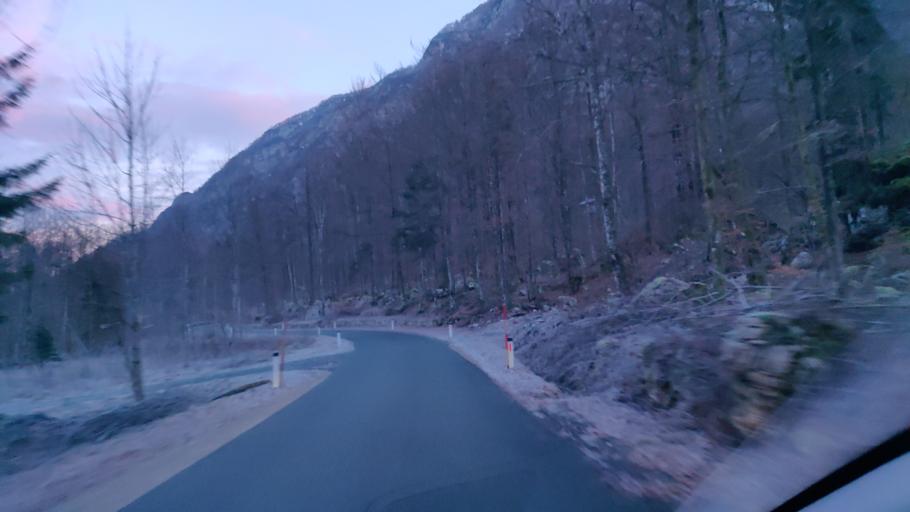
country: SI
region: Tolmin
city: Tolmin
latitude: 46.2771
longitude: 13.8183
